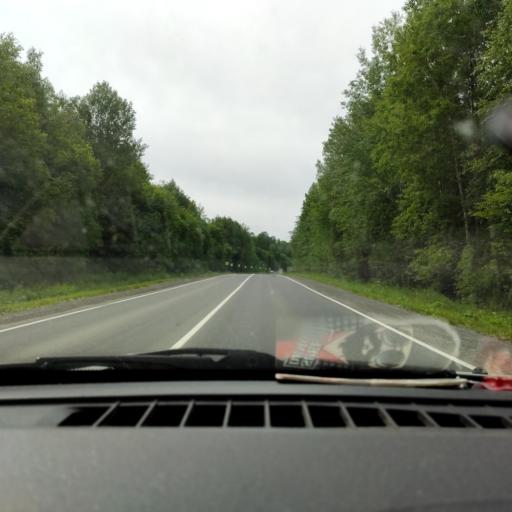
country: RU
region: Perm
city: Chusovoy
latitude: 58.3838
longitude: 57.9207
